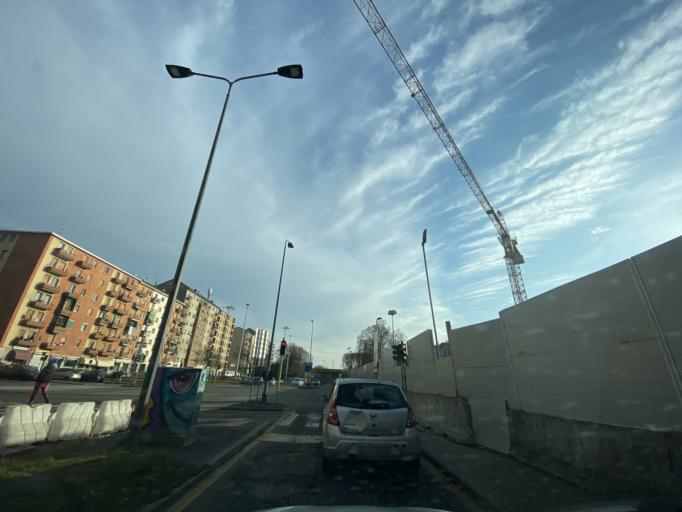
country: IT
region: Lombardy
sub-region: Citta metropolitana di Milano
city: Romano Banco
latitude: 45.4499
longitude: 9.1356
